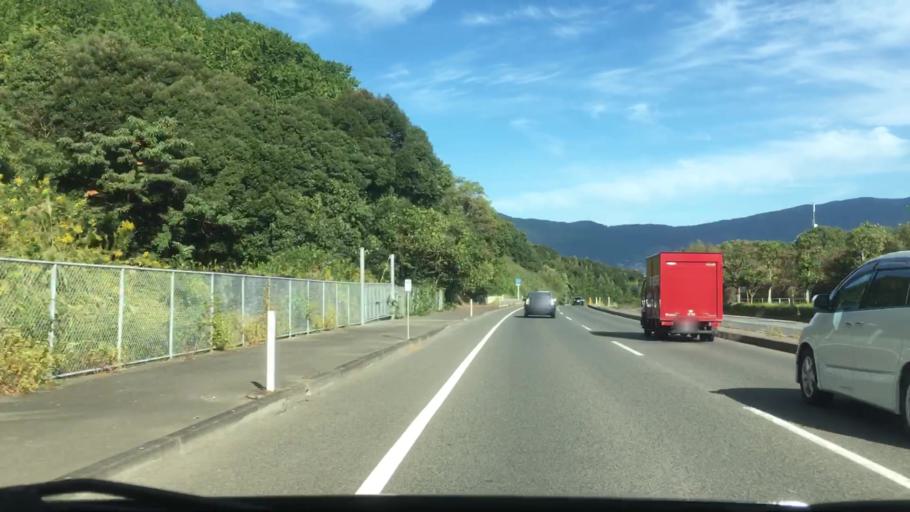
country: JP
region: Nagasaki
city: Sasebo
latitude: 33.1281
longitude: 129.7879
